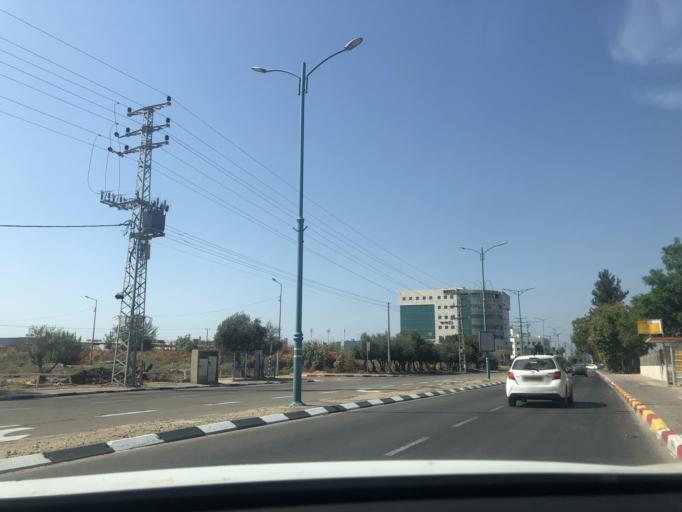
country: IL
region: Central District
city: Lod
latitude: 31.9616
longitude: 34.8993
